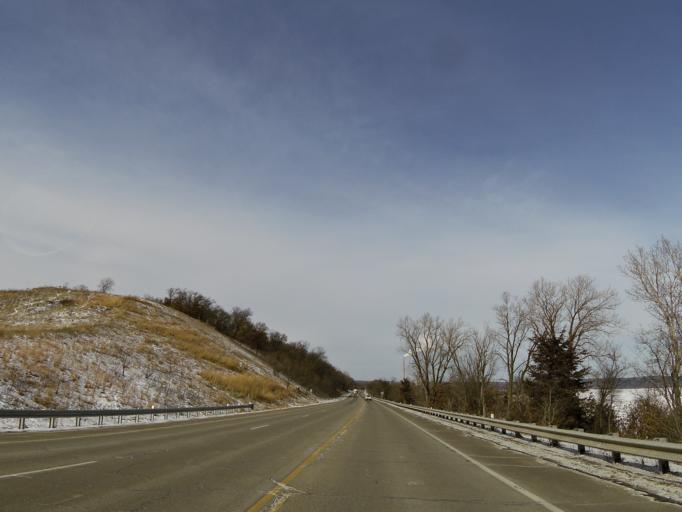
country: US
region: Wisconsin
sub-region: Saint Croix County
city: North Hudson
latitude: 44.9946
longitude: -92.7779
